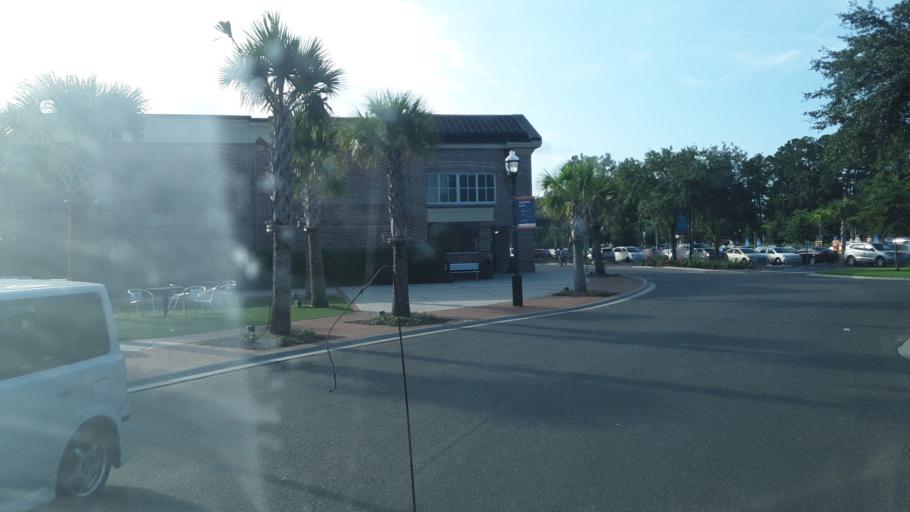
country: US
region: South Carolina
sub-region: Beaufort County
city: Bluffton
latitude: 32.2687
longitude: -80.8591
